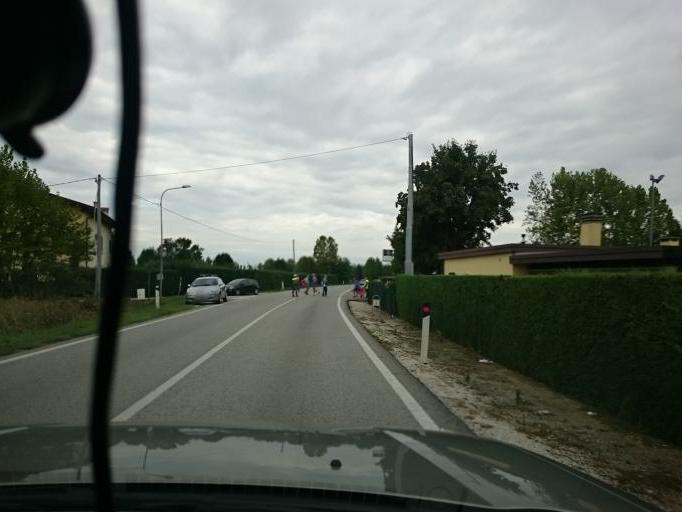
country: IT
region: Veneto
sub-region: Provincia di Padova
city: Selvazzano Dentro
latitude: 45.3850
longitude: 11.7787
